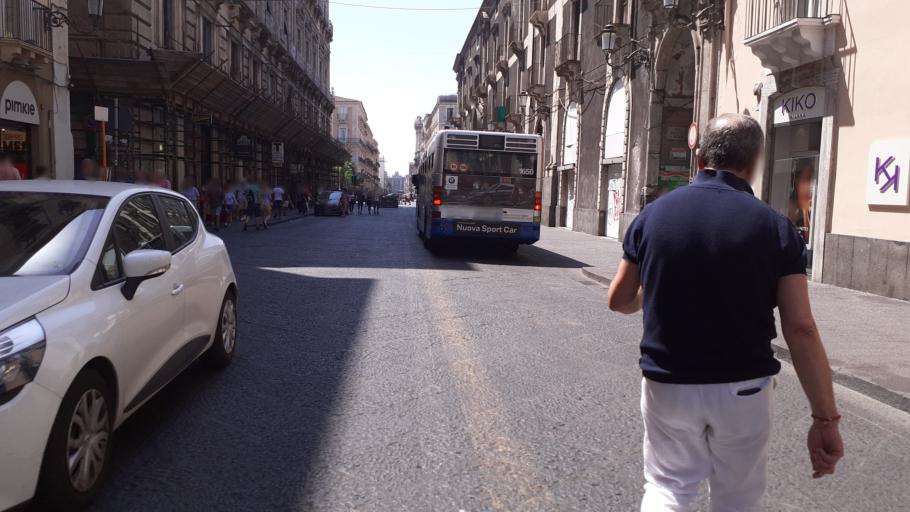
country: IT
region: Sicily
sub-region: Catania
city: Catania
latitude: 37.5085
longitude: 15.0860
